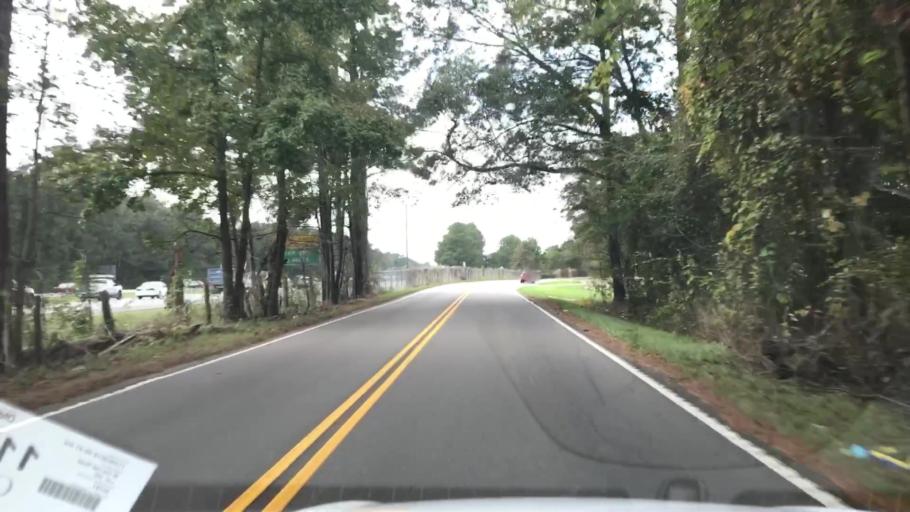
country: US
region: South Carolina
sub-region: Berkeley County
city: Ladson
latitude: 33.0082
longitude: -80.1064
